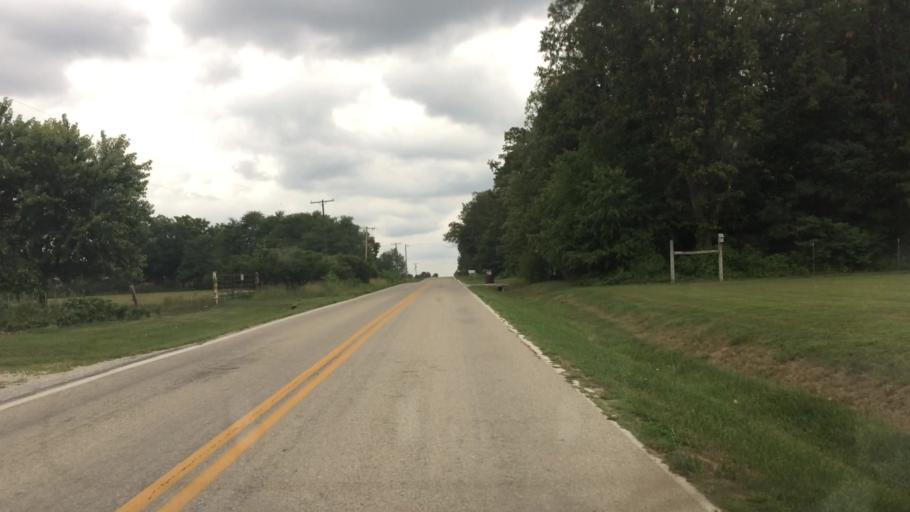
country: US
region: Missouri
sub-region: Greene County
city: Strafford
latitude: 37.3003
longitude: -93.1543
